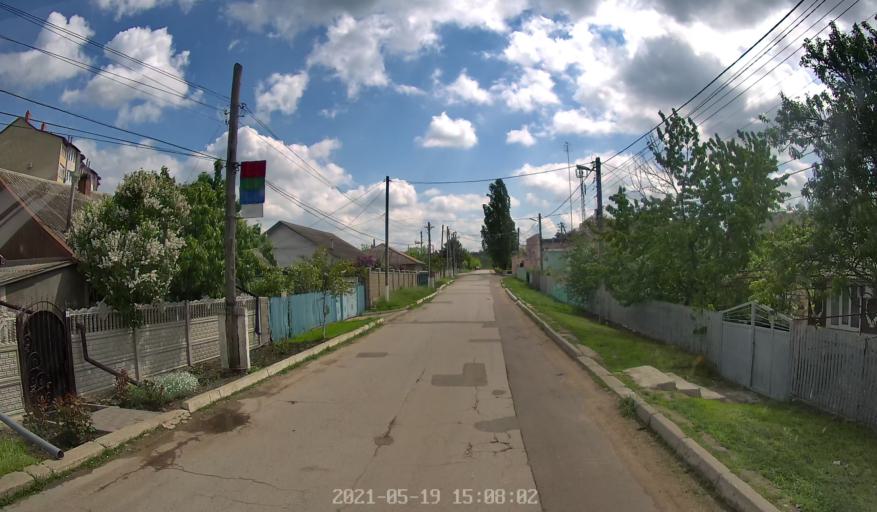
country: MD
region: Chisinau
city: Stauceni
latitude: 47.0621
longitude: 28.9484
